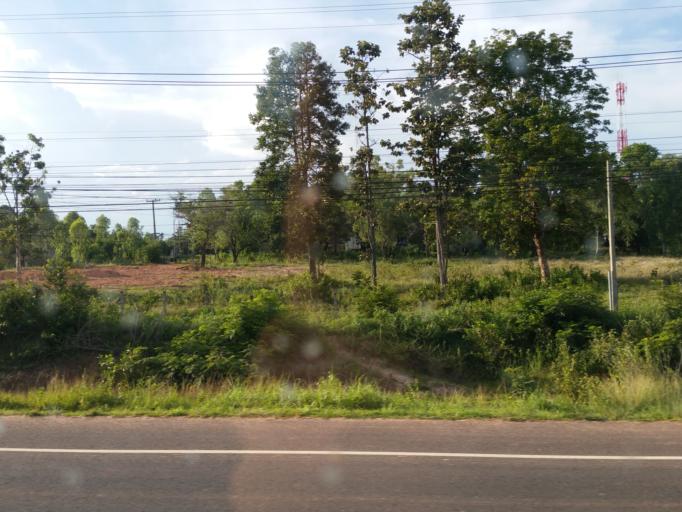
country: TH
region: Changwat Ubon Ratchathani
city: Sirindhorn
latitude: 15.2010
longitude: 105.3818
